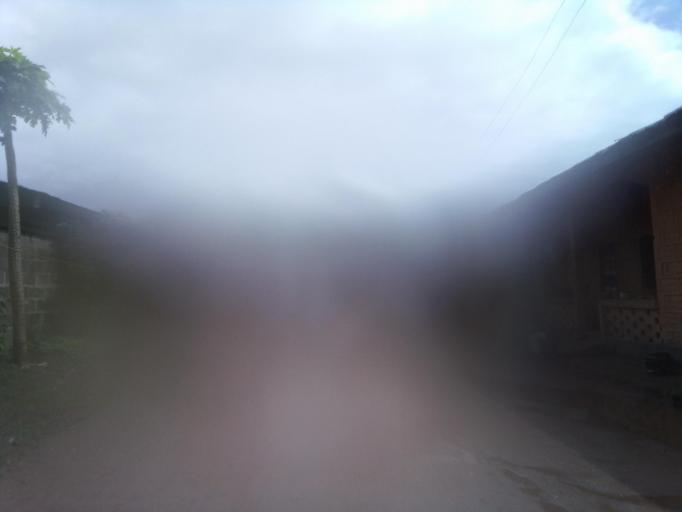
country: SL
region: Eastern Province
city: Kenema
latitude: 7.8811
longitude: -11.1843
